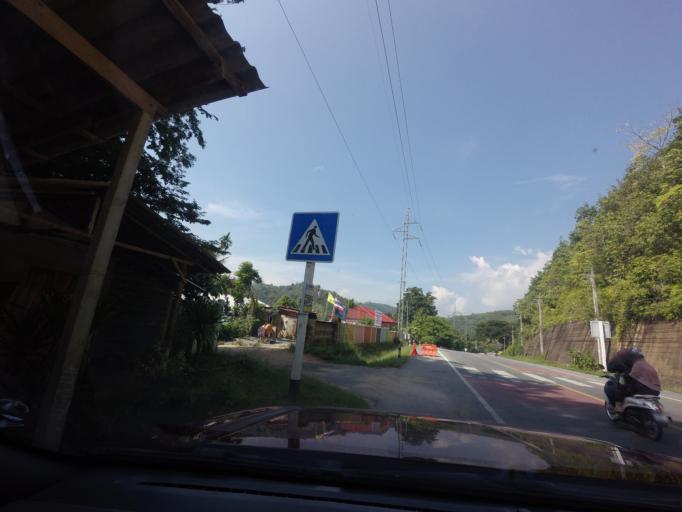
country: TH
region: Yala
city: Than To
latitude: 5.9622
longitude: 101.1949
